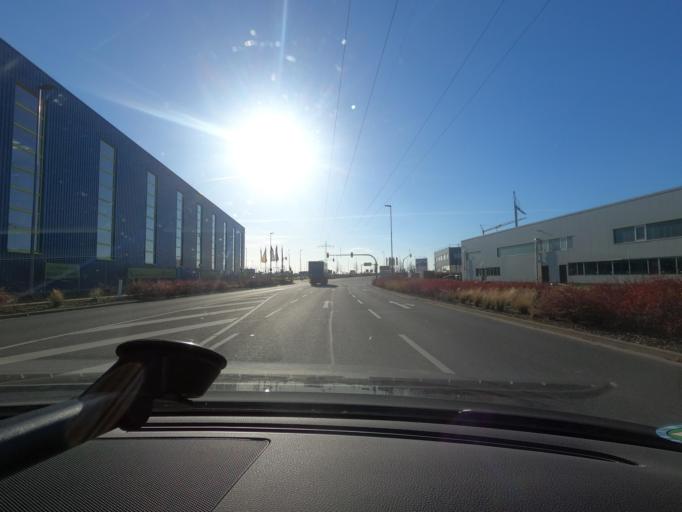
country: DE
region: North Rhine-Westphalia
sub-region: Regierungsbezirk Dusseldorf
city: Kaarst
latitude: 51.2136
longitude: 6.6398
